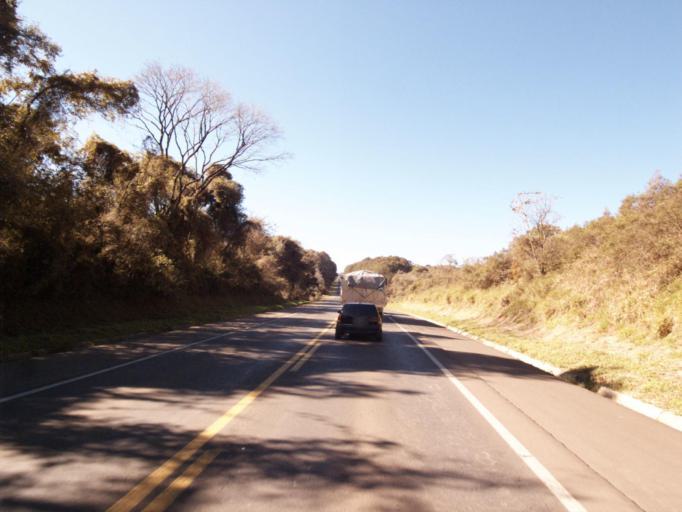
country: BR
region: Santa Catarina
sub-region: Xanxere
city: Xanxere
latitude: -26.9138
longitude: -52.4766
